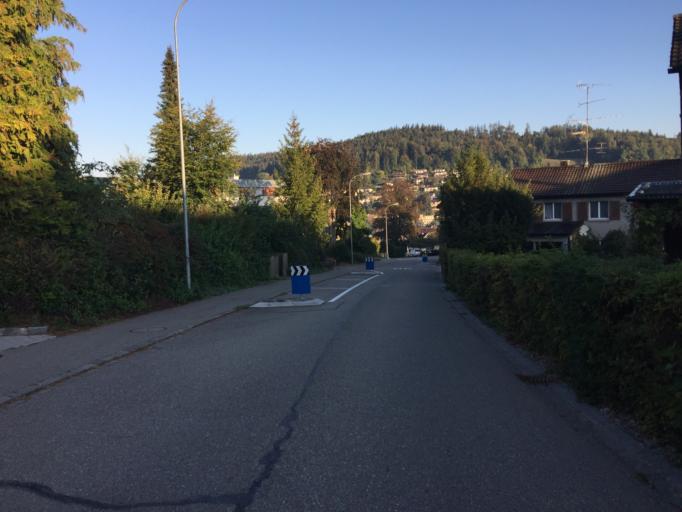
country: CH
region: Saint Gallen
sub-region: Wahlkreis Wil
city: Oberuzwil
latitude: 47.4274
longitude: 9.1270
